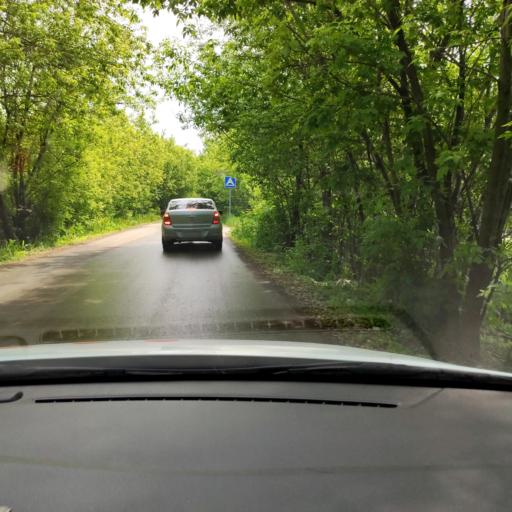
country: RU
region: Tatarstan
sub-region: Gorod Kazan'
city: Kazan
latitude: 55.7018
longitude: 49.0872
